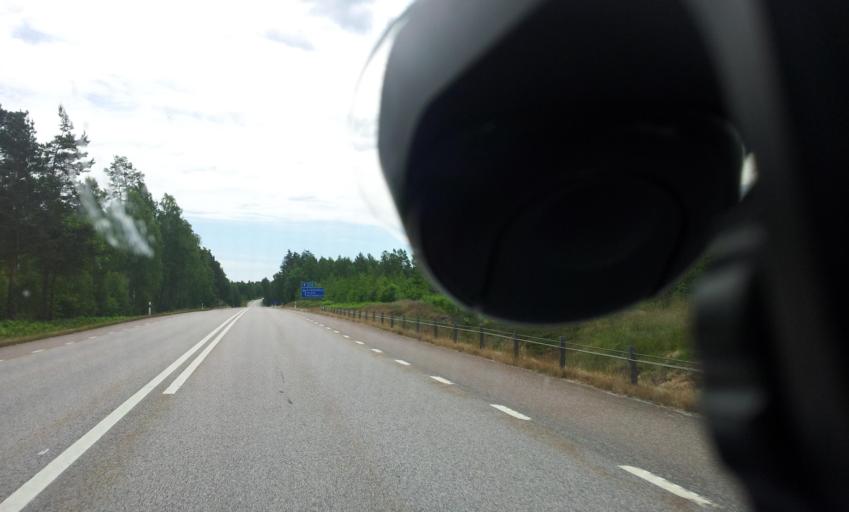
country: SE
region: Kalmar
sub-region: Oskarshamns Kommun
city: Oskarshamn
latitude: 57.4985
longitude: 16.5075
